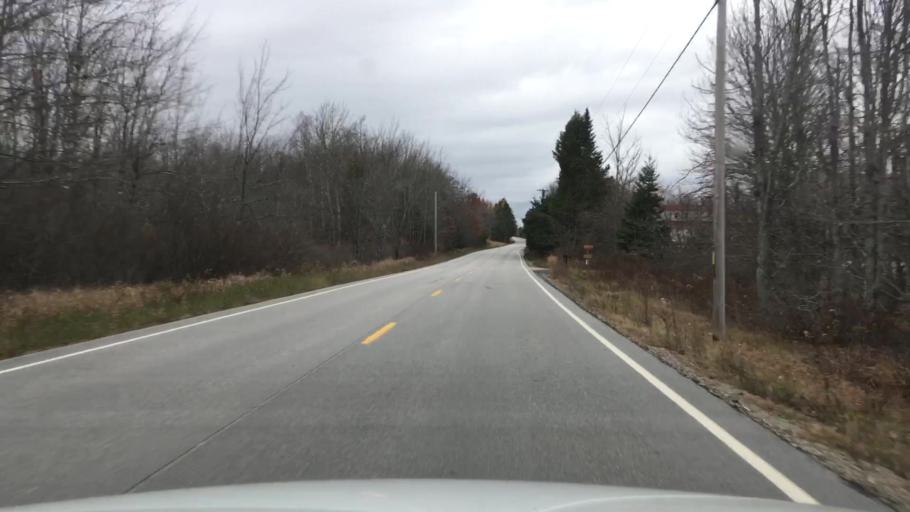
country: US
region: Maine
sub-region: Hancock County
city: Penobscot
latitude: 44.4722
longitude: -68.6368
